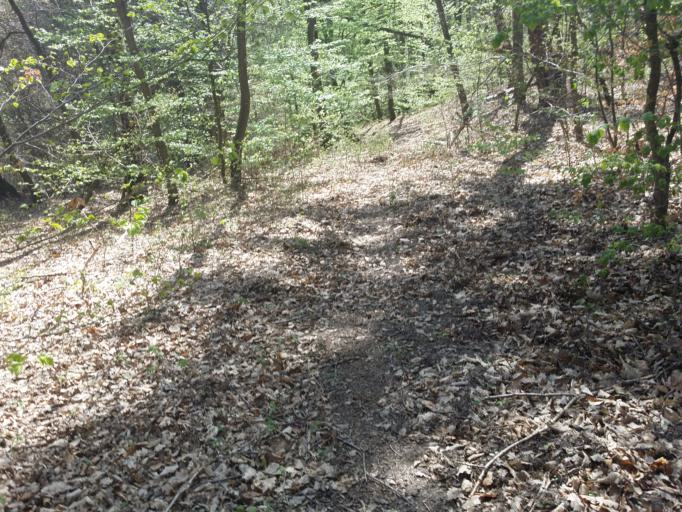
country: DE
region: Saxony-Anhalt
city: Gernrode
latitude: 51.7181
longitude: 11.1493
